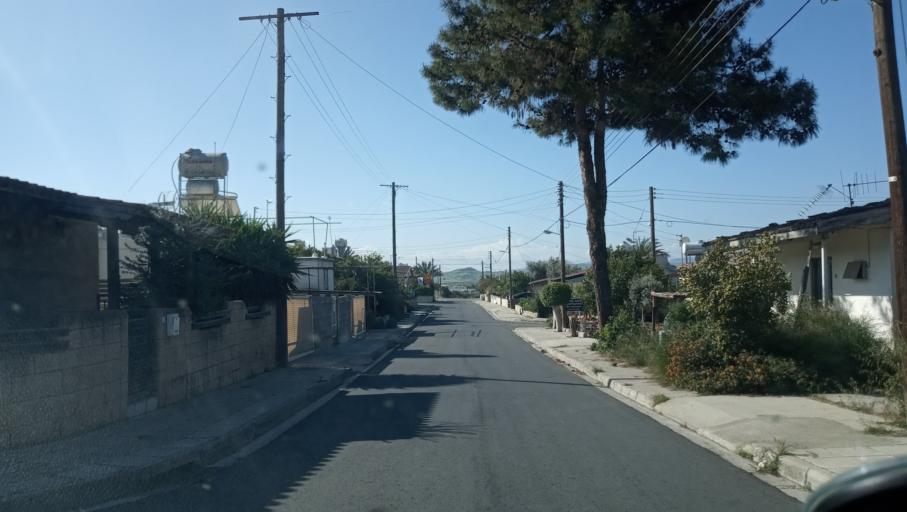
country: CY
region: Lefkosia
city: Tseri
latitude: 35.0736
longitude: 33.3299
